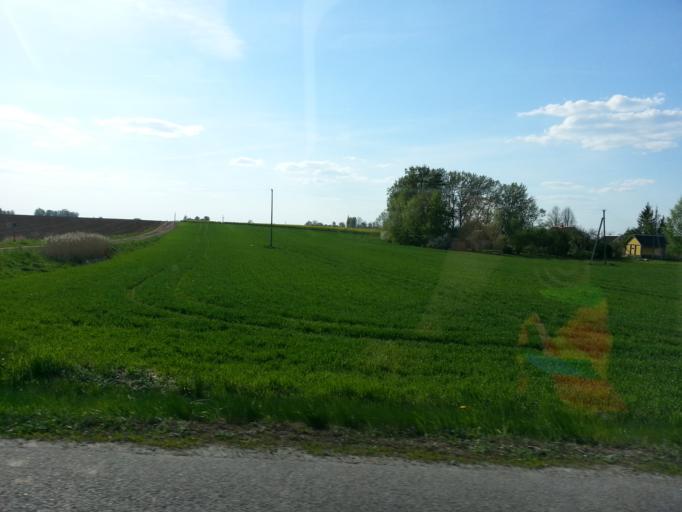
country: LT
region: Panevezys
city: Pasvalys
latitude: 56.0124
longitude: 24.3559
